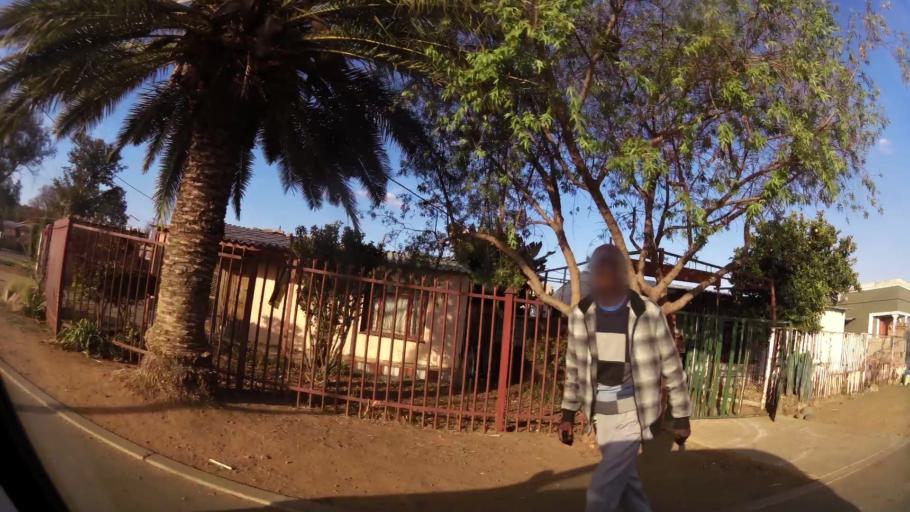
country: ZA
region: Gauteng
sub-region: City of Tshwane Metropolitan Municipality
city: Cullinan
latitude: -25.7118
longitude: 28.3687
